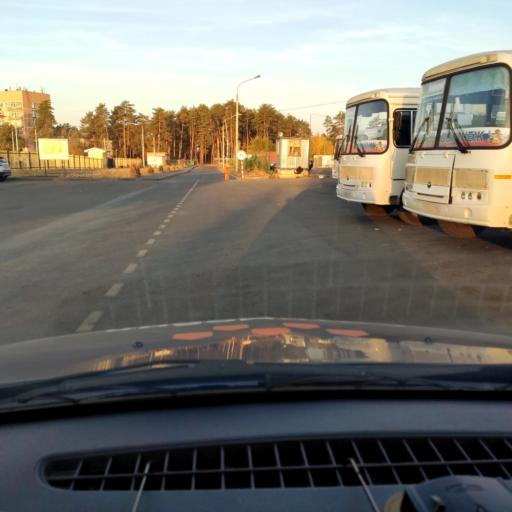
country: RU
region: Voronezj
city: Maslovka
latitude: 51.5872
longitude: 39.2453
